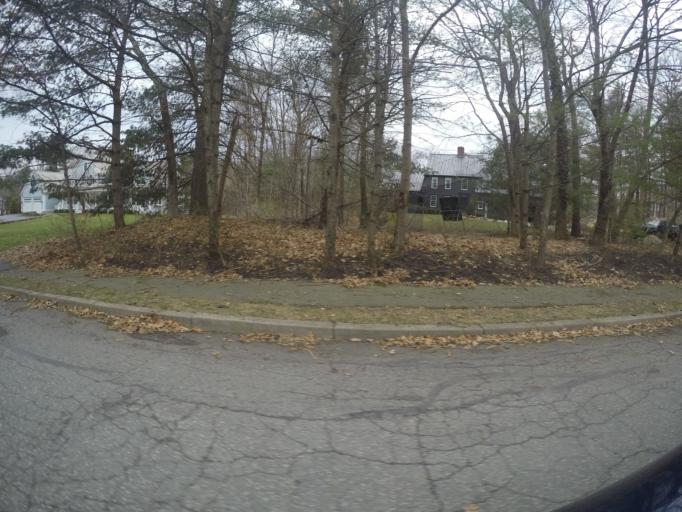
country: US
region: Massachusetts
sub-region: Norfolk County
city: Stoughton
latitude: 42.0823
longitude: -71.1079
